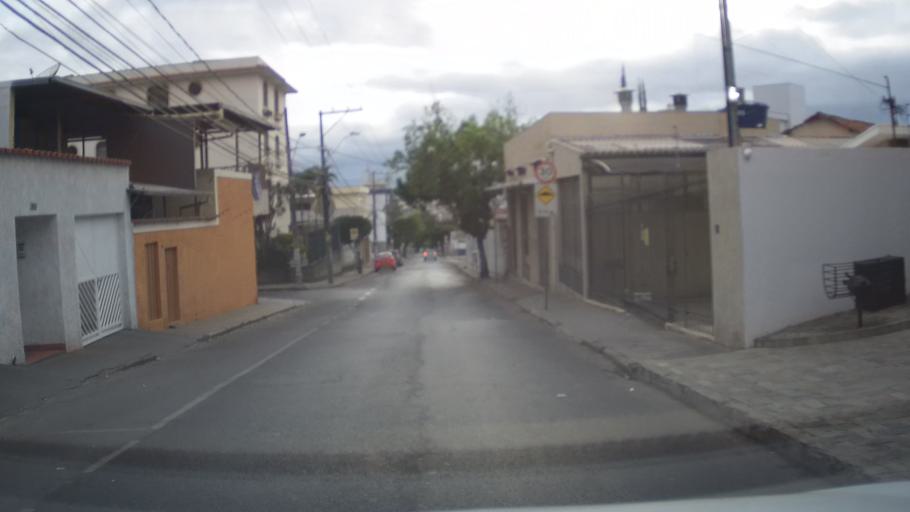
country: BR
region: Minas Gerais
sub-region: Belo Horizonte
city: Belo Horizonte
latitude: -19.9064
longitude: -43.9694
